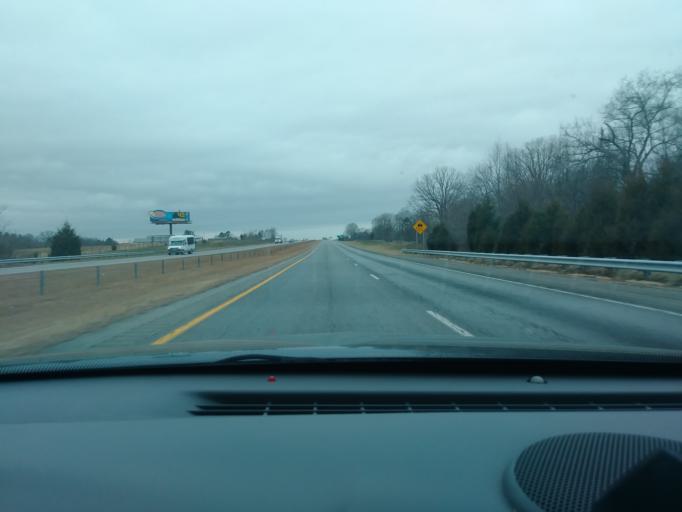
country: US
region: North Carolina
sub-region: Yadkin County
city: Yadkinville
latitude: 36.1177
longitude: -80.7820
